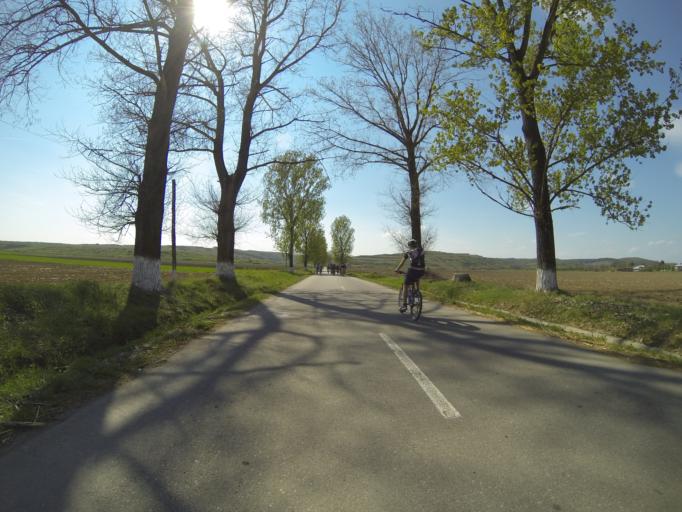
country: RO
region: Gorj
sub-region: Comuna Crusetu
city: Crusetu
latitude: 44.6209
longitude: 23.6805
